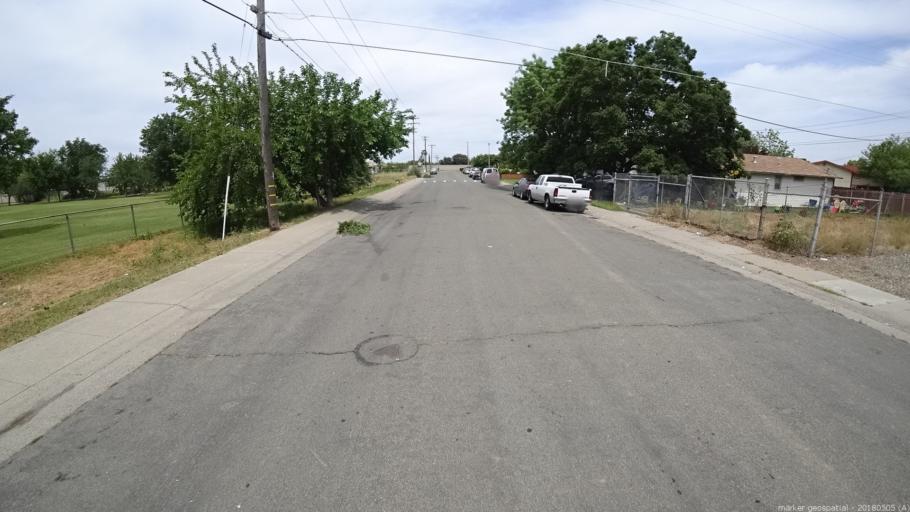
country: US
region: California
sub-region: Sacramento County
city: Rio Linda
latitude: 38.6414
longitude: -121.4361
